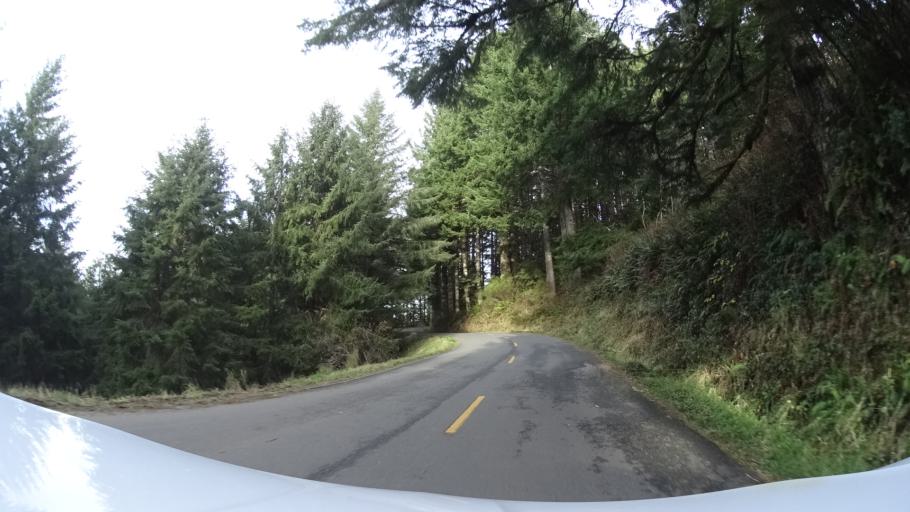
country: US
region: California
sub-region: Humboldt County
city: Ferndale
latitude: 40.5160
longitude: -124.2704
